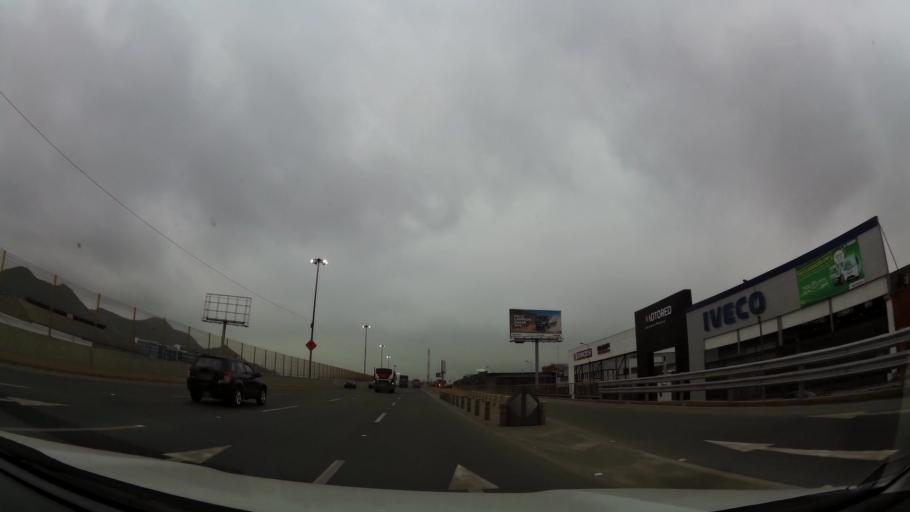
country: PE
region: Lima
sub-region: Lima
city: San Luis
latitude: -12.0609
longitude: -76.9722
